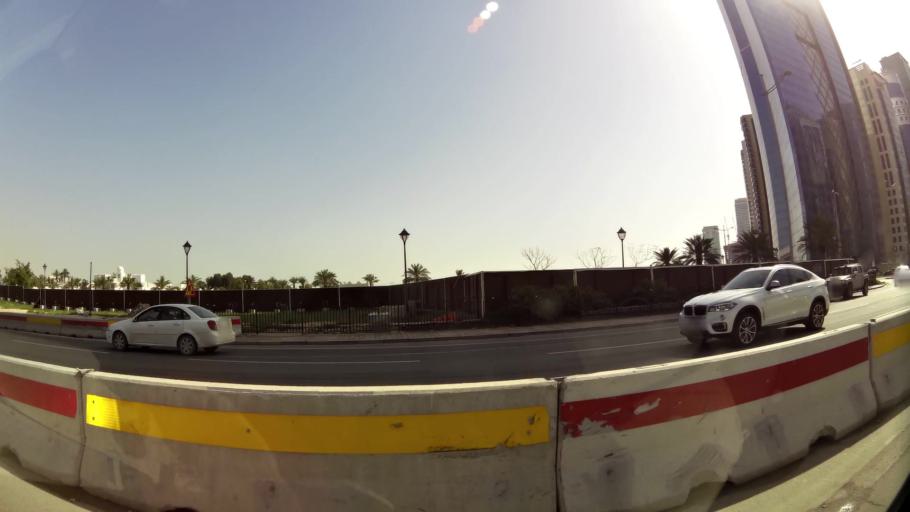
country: QA
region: Baladiyat ad Dawhah
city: Doha
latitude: 25.3304
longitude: 51.5230
